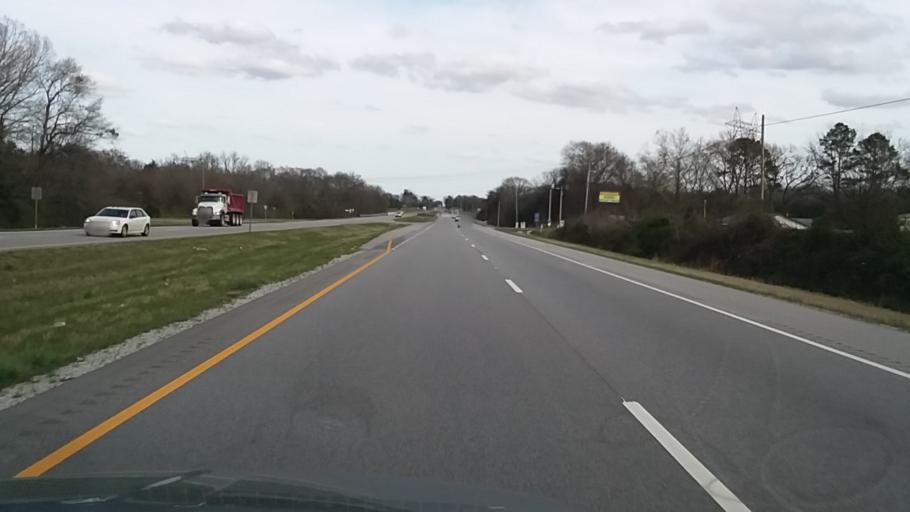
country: US
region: Alabama
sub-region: Lawrence County
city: Town Creek
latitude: 34.6823
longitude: -87.4559
